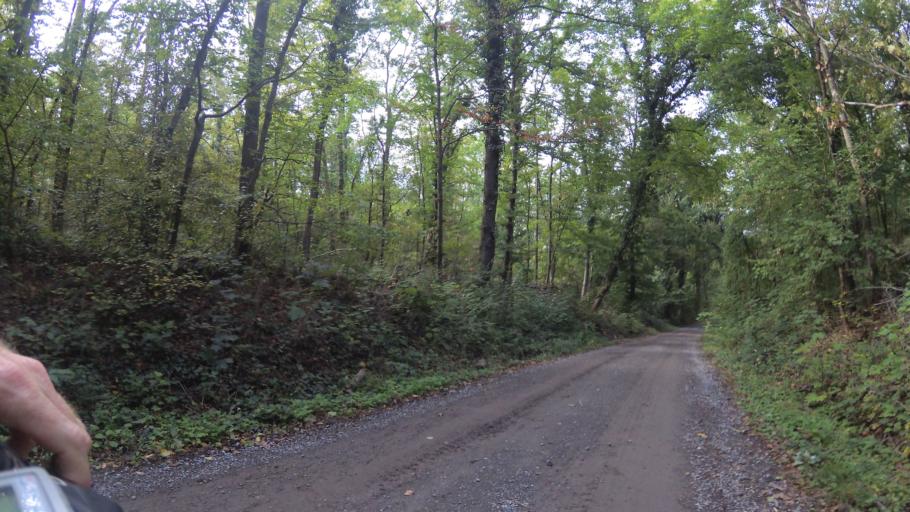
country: DE
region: Baden-Wuerttemberg
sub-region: Regierungsbezirk Stuttgart
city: Erlenbach
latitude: 49.2077
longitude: 9.2813
